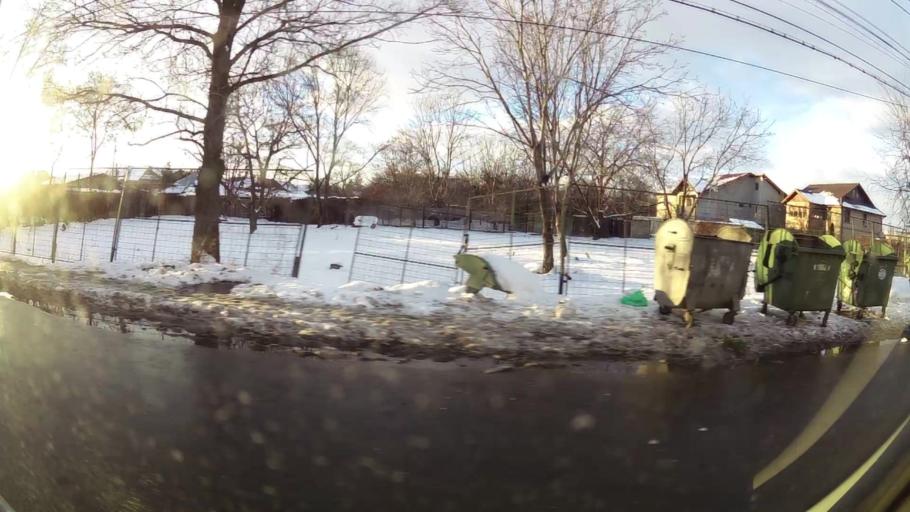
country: RO
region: Ilfov
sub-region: Comuna Popesti-Leordeni
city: Popesti-Leordeni
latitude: 44.3718
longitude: 26.1360
